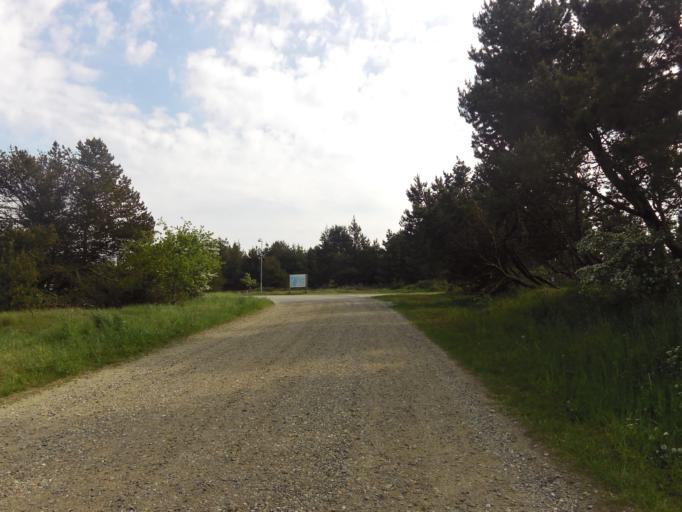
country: DE
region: Schleswig-Holstein
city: List
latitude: 55.1630
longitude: 8.5492
